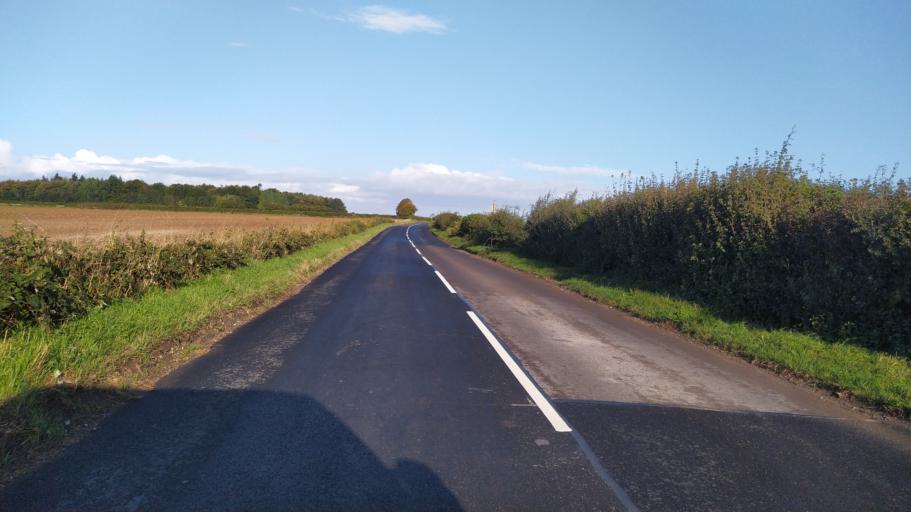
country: GB
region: England
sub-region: Dorset
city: Wimborne Minster
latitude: 50.8864
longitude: -1.9991
